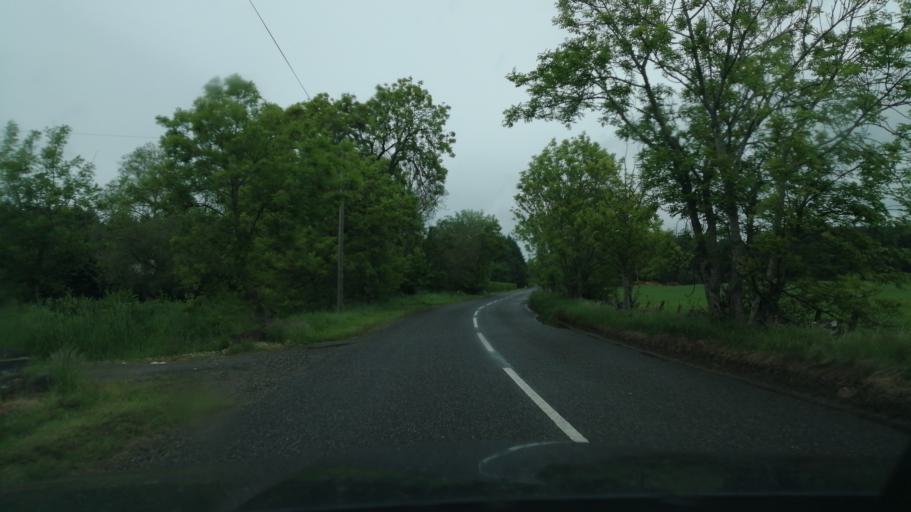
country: GB
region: Scotland
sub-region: Aberdeenshire
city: Portsoy
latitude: 57.6205
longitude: -2.7221
